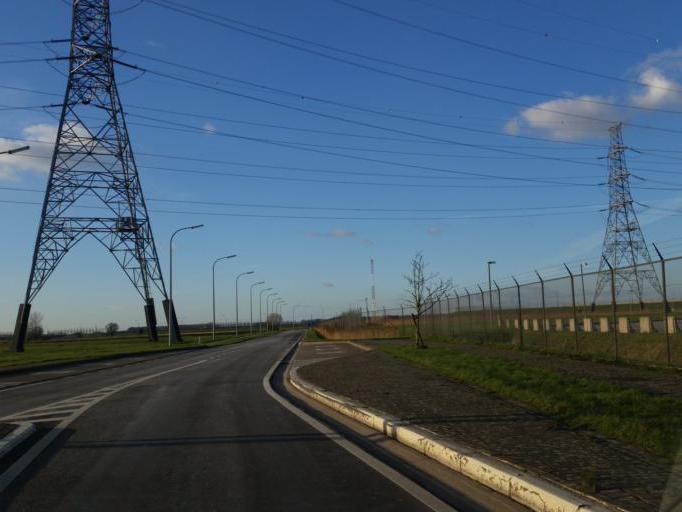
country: BE
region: Flanders
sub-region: Provincie Oost-Vlaanderen
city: Beveren
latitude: 51.3198
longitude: 4.2542
